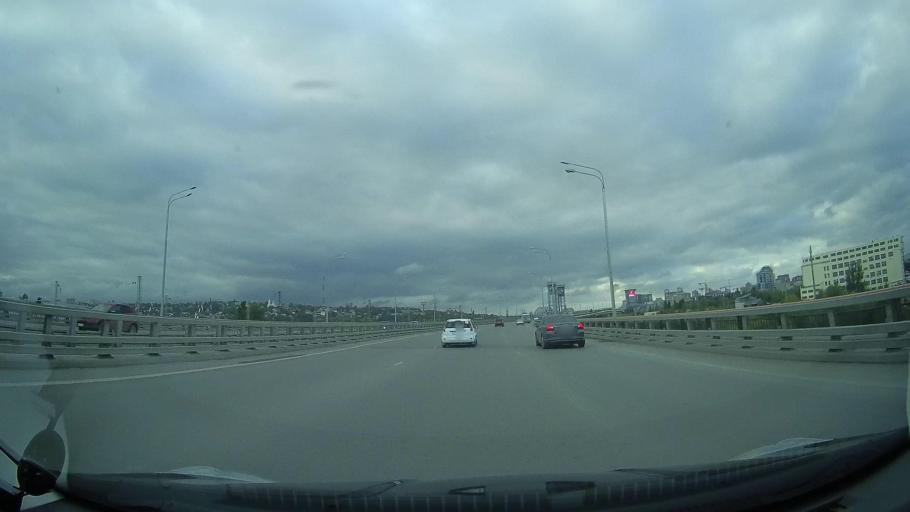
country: RU
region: Rostov
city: Rostov-na-Donu
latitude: 47.2049
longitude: 39.7079
